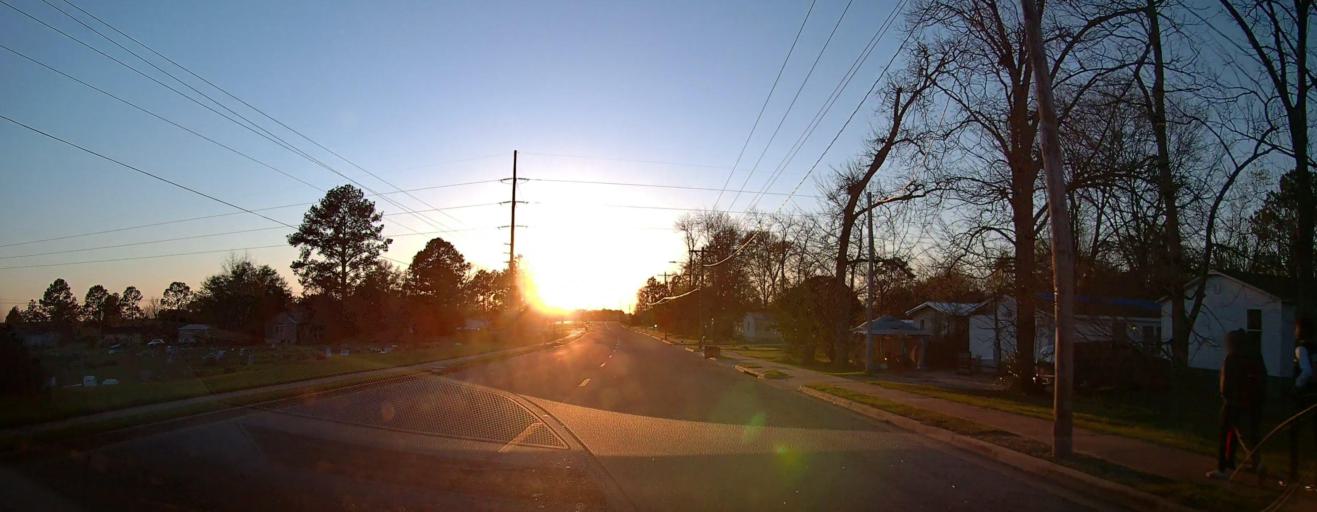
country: US
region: Georgia
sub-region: Crisp County
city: Cordele
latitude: 31.9553
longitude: -83.7916
